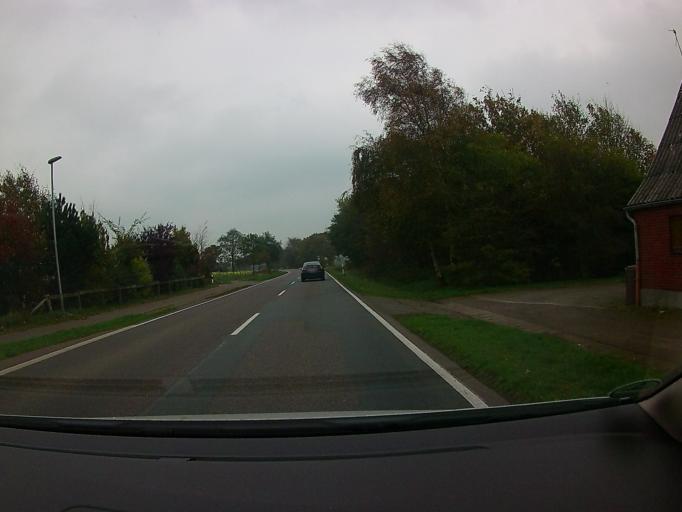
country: DE
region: Schleswig-Holstein
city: Goldebek
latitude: 54.6760
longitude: 9.1293
